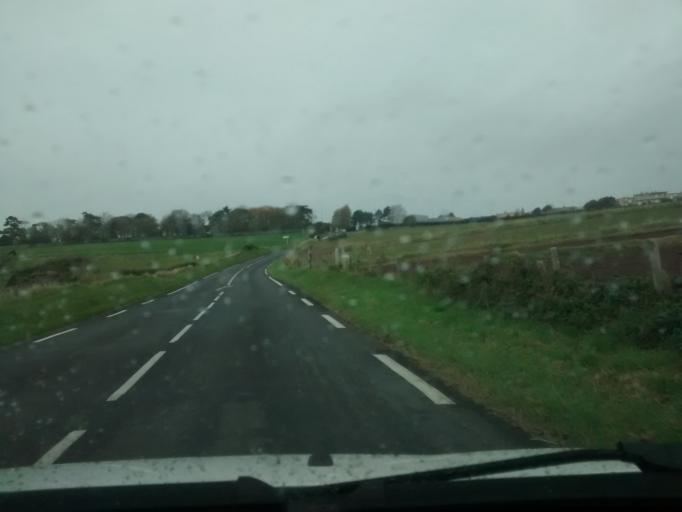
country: FR
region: Lower Normandy
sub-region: Departement de la Manche
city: Saint-Pair-sur-Mer
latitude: 48.8251
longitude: -1.5771
